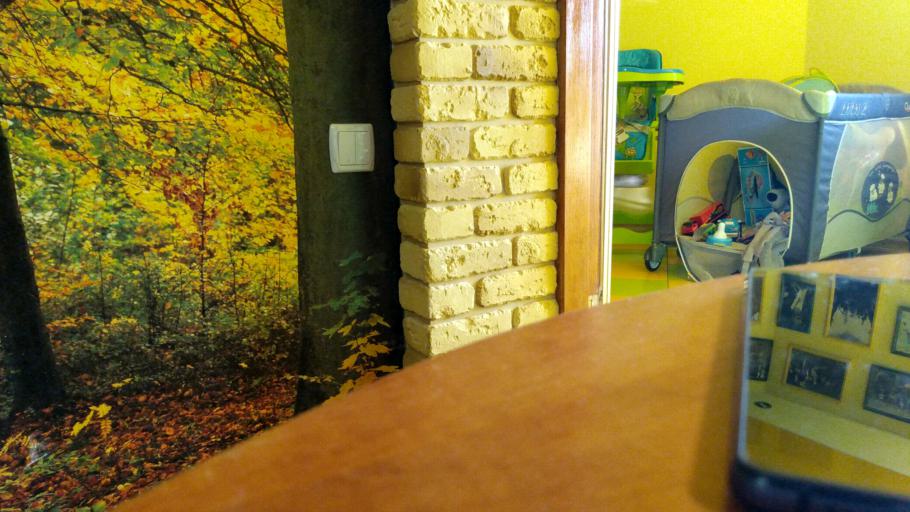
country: RU
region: Tverskaya
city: Kalashnikovo
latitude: 57.2862
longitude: 35.3661
